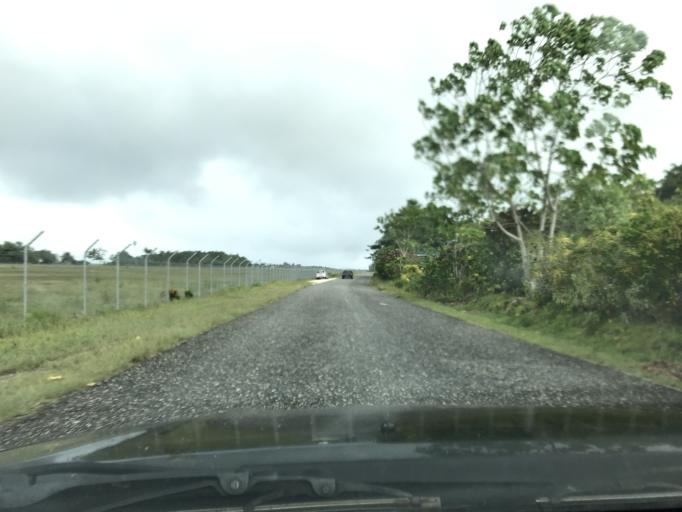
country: SB
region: Western Province
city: Gizo
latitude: -8.3255
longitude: 157.2660
